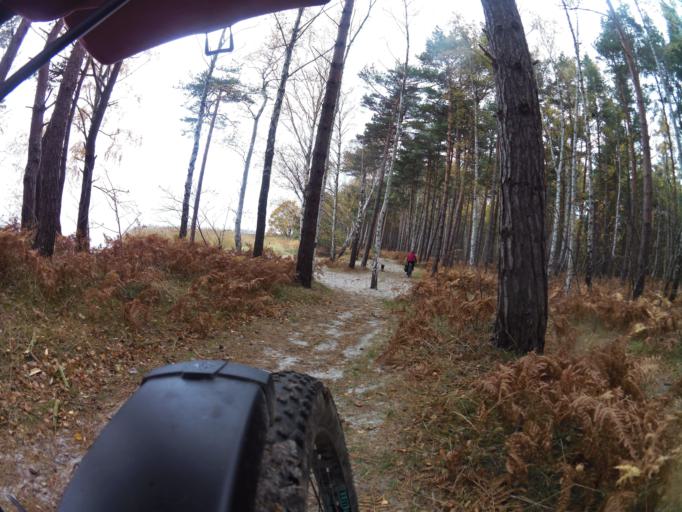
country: PL
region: Pomeranian Voivodeship
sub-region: Powiat pucki
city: Jastarnia
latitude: 54.6865
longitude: 18.7044
